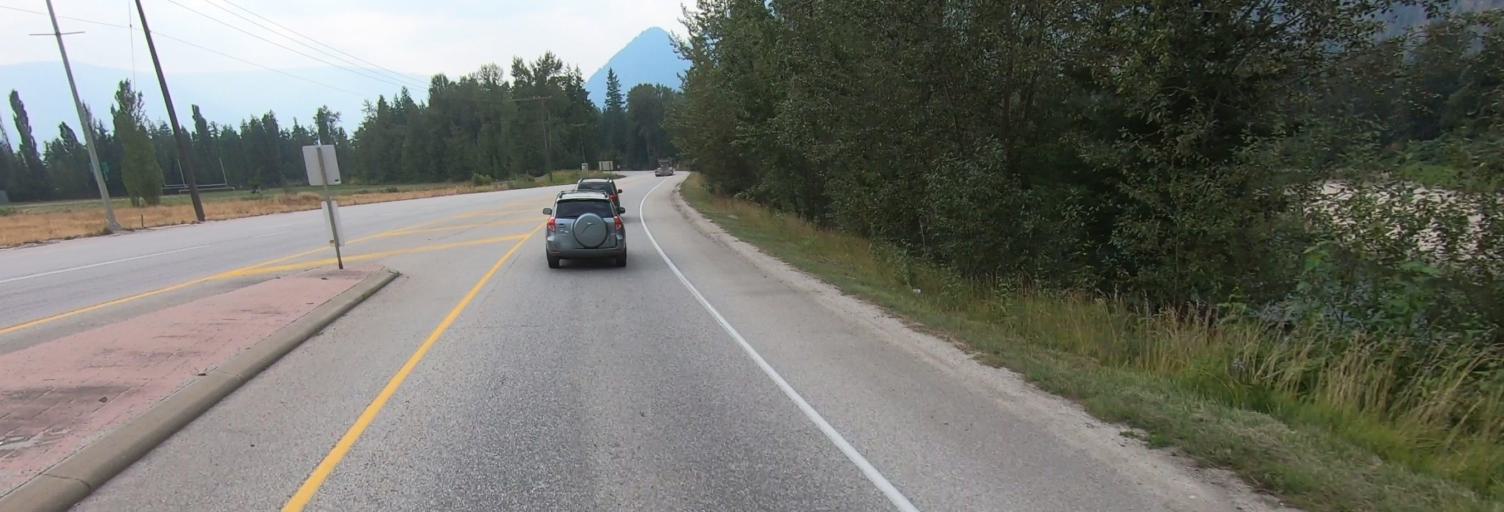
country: CA
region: British Columbia
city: Sicamous
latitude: 50.8383
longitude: -118.9769
